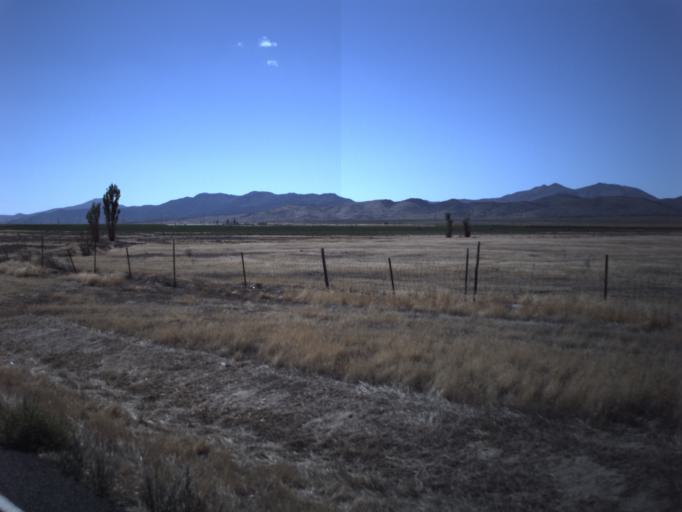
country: US
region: Utah
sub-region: Utah County
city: Genola
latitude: 40.0248
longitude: -111.9583
